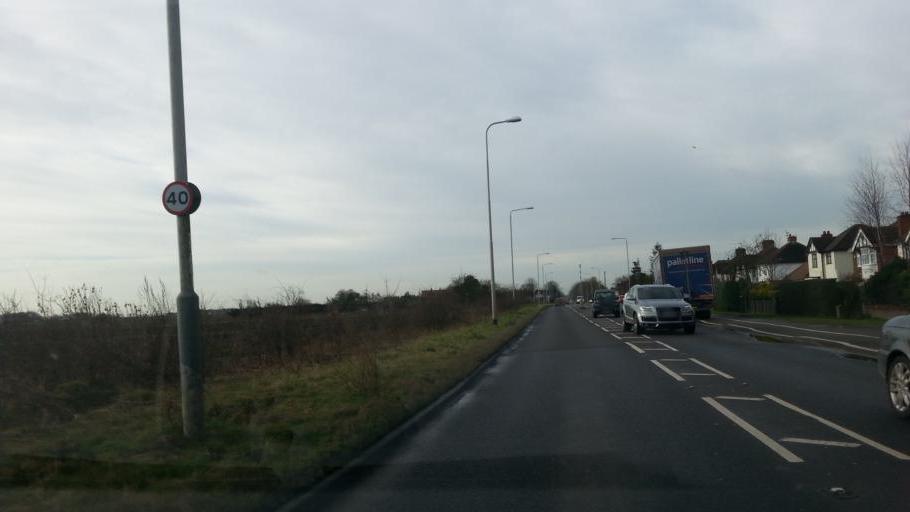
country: GB
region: England
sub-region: Nottinghamshire
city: Farndon
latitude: 53.0629
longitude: -0.8380
